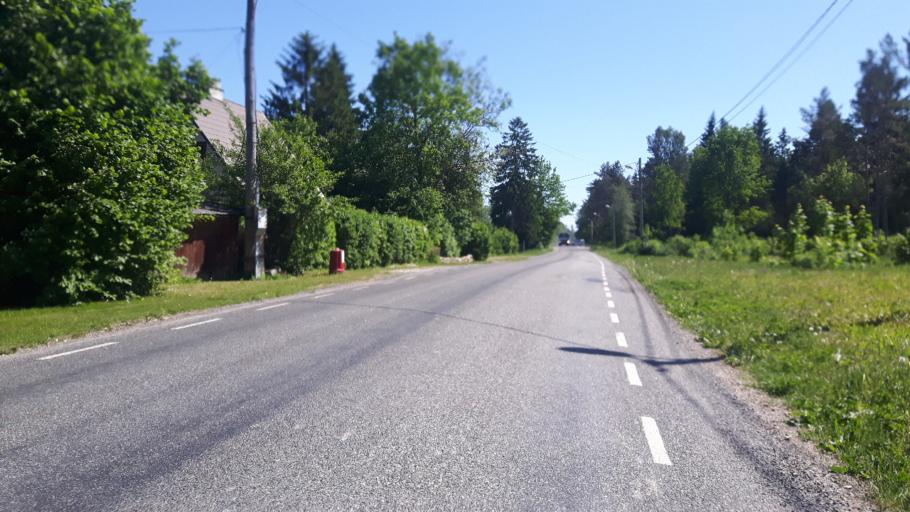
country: EE
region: Raplamaa
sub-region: Kohila vald
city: Kohila
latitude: 59.1748
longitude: 24.7325
